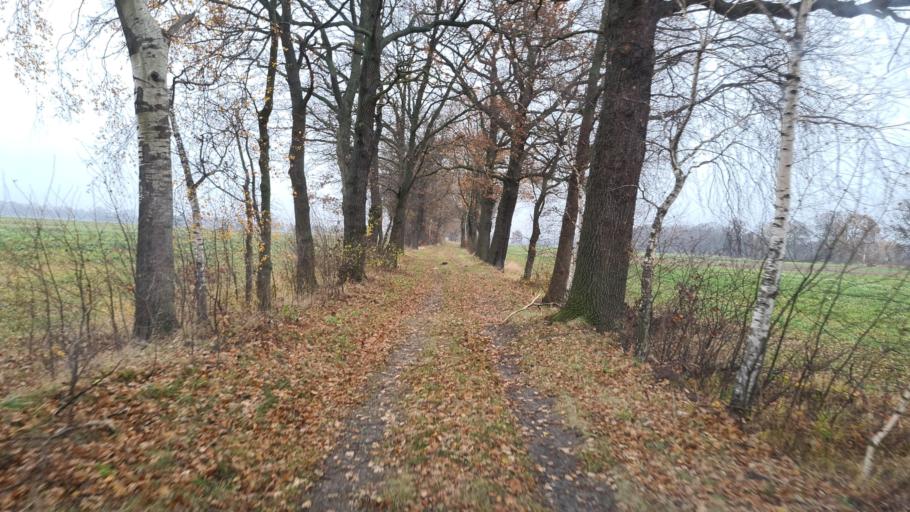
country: DE
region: Brandenburg
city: Schraden
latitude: 51.4121
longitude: 13.7107
